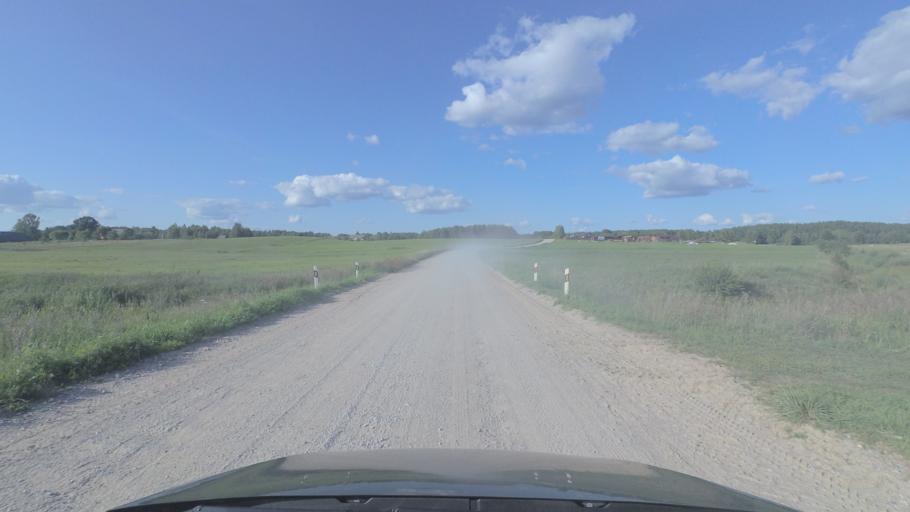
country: LT
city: Pabrade
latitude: 55.1343
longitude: 25.7076
